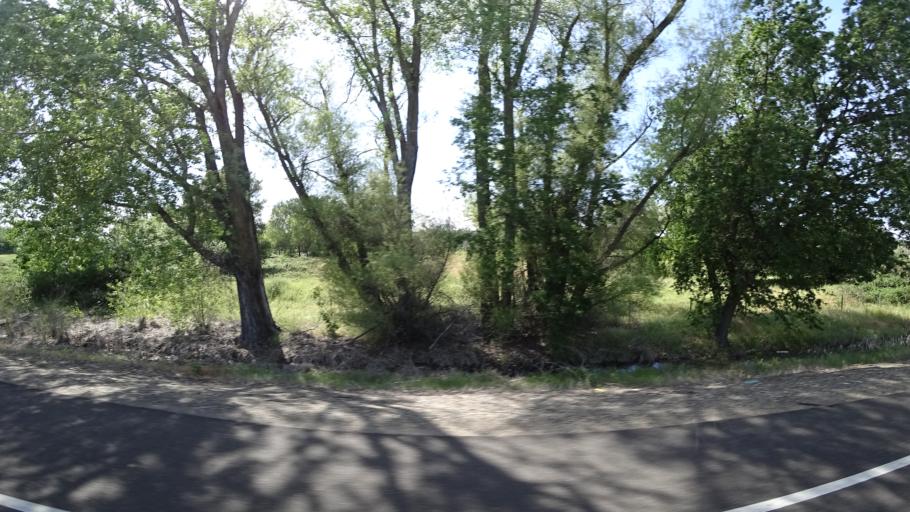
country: US
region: California
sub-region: Shasta County
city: Cottonwood
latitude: 40.3946
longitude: -122.2846
